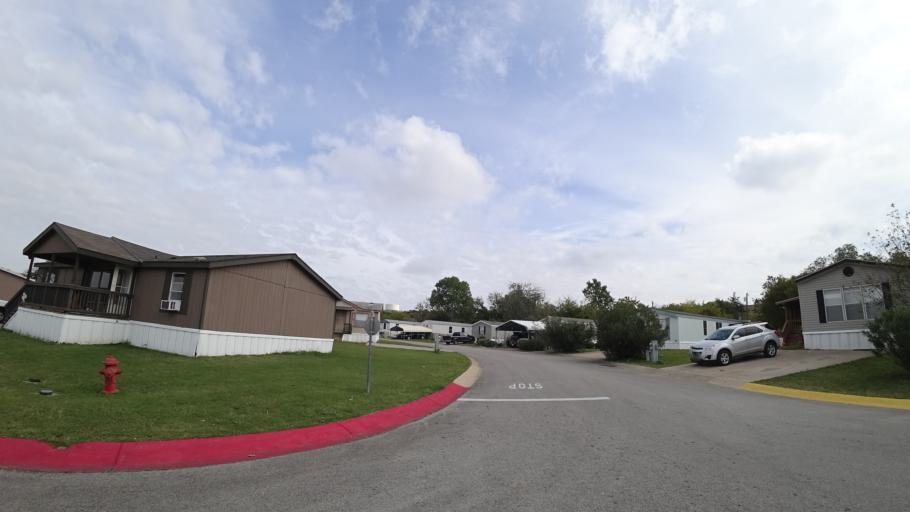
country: US
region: Texas
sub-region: Williamson County
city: Round Rock
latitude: 30.4875
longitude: -97.6905
